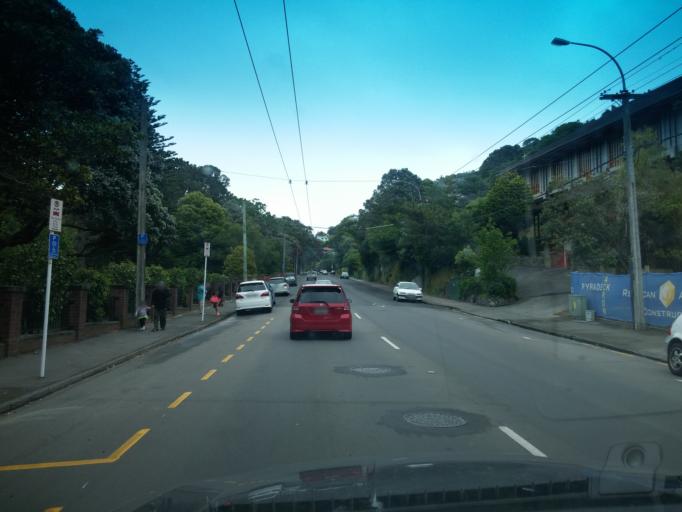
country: NZ
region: Wellington
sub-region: Wellington City
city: Kelburn
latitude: -41.2809
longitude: 174.7666
